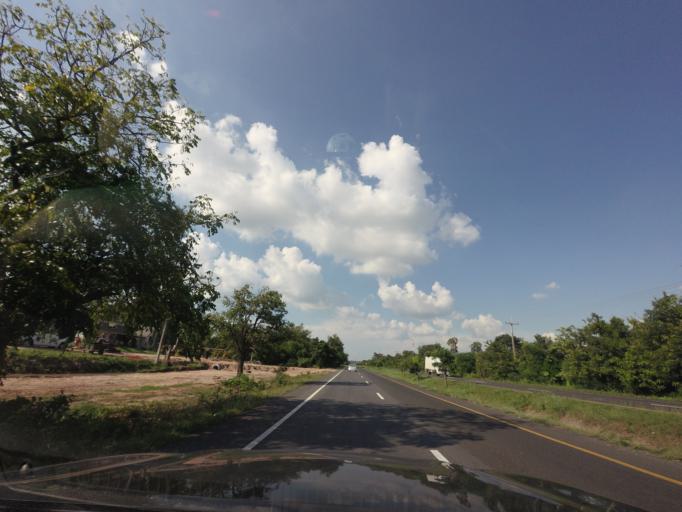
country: TH
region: Nakhon Ratchasima
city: Bua Lai
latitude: 15.6730
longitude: 102.5756
